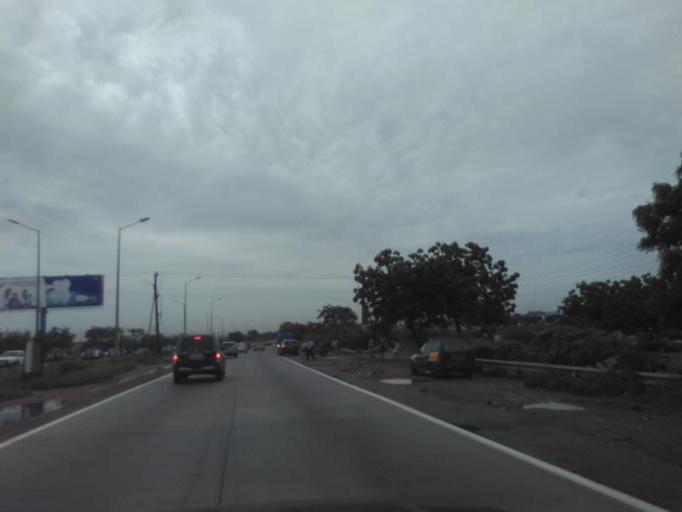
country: GH
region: Greater Accra
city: Tema
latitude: 5.6743
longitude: -0.0445
